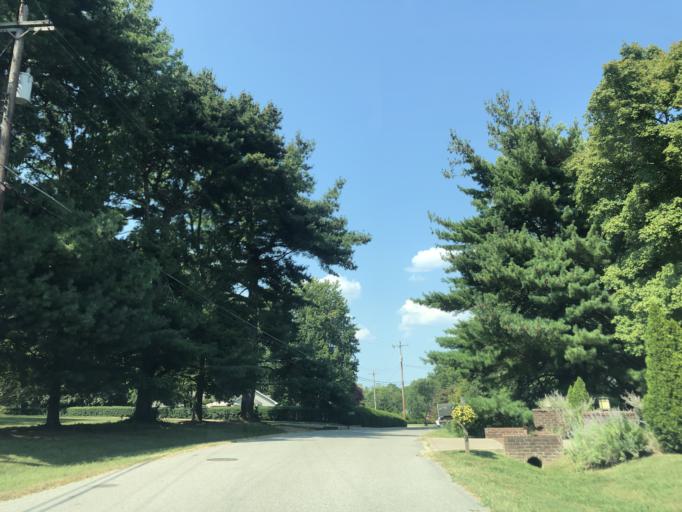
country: US
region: Tennessee
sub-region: Davidson County
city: Oak Hill
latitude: 36.0894
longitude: -86.7656
